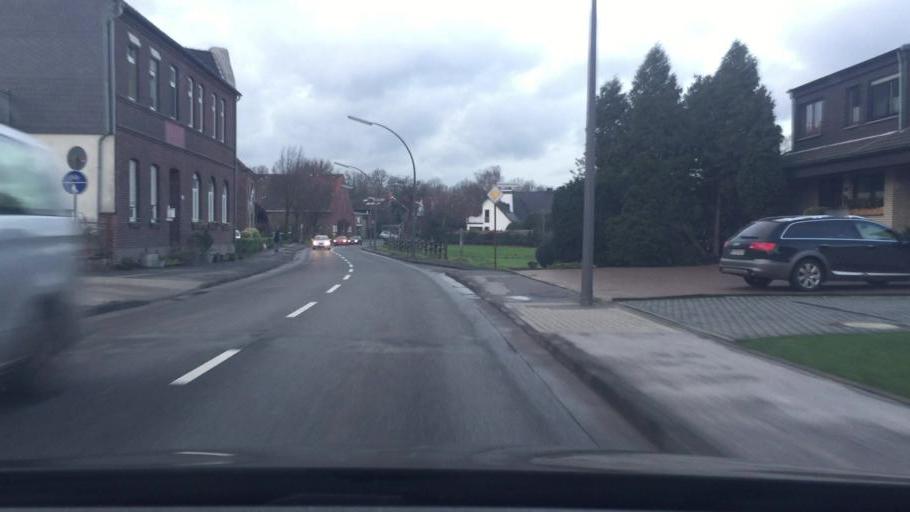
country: DE
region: North Rhine-Westphalia
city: Oer-Erkenschwick
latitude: 51.6213
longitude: 7.2531
